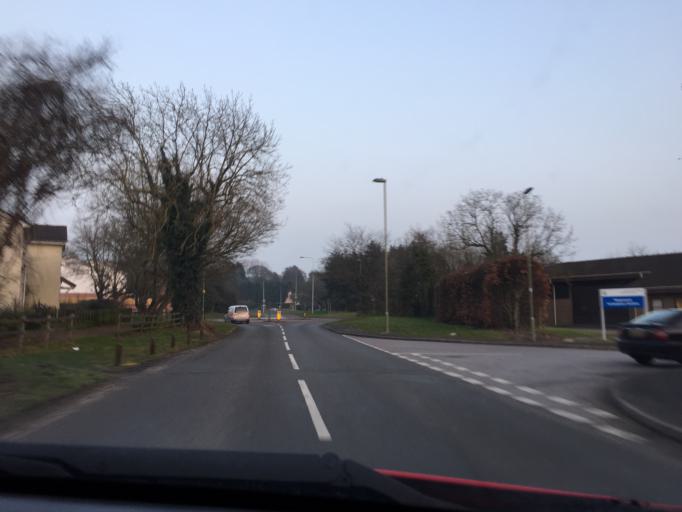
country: GB
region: England
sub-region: Hampshire
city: Ringwood
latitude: 50.8502
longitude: -1.7679
